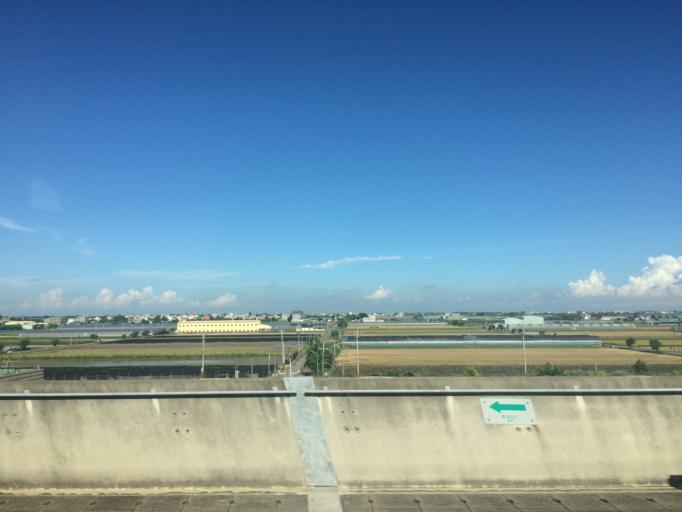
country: TW
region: Taiwan
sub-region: Chiayi
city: Taibao
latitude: 23.5177
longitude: 120.3267
